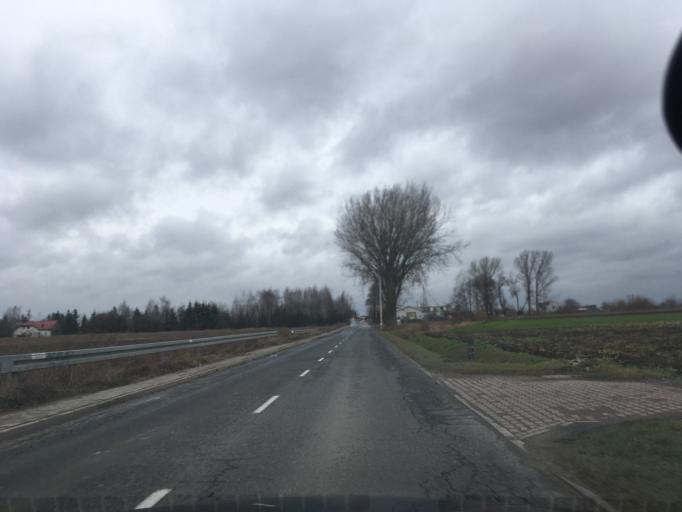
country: PL
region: Masovian Voivodeship
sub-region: Powiat piaseczynski
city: Lesznowola
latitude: 52.0981
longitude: 20.9331
